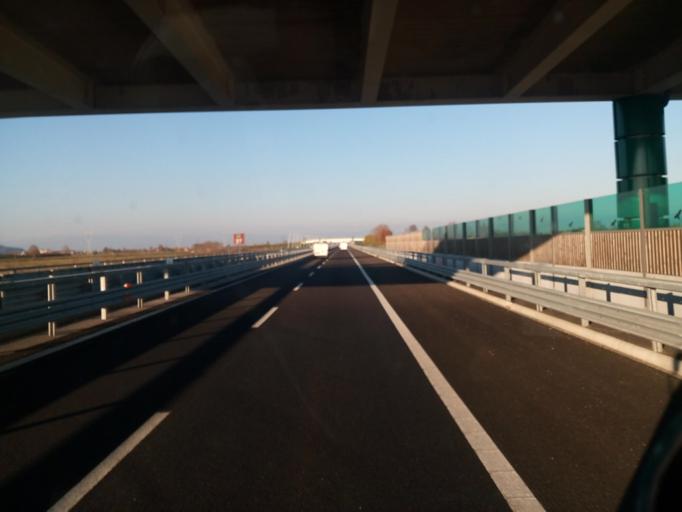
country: IT
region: Veneto
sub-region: Provincia di Vicenza
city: Villaganzerla
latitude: 45.4132
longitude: 11.6339
